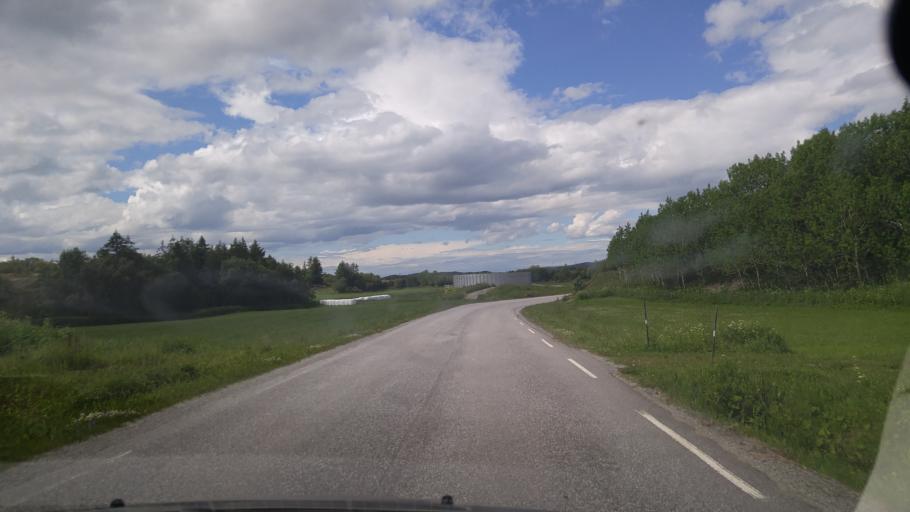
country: NO
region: Nord-Trondelag
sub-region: Vikna
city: Rorvik
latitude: 64.9038
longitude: 11.1454
